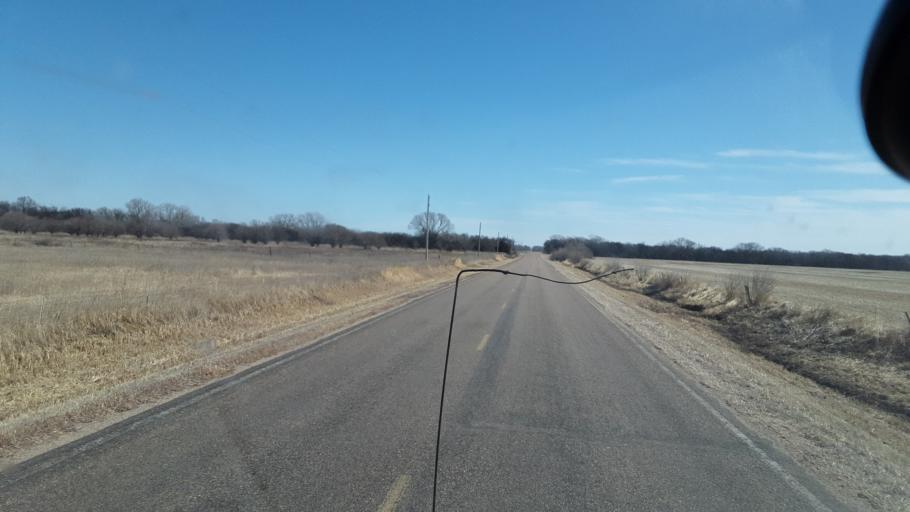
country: US
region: Kansas
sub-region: Reno County
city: Nickerson
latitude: 38.2175
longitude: -98.0681
